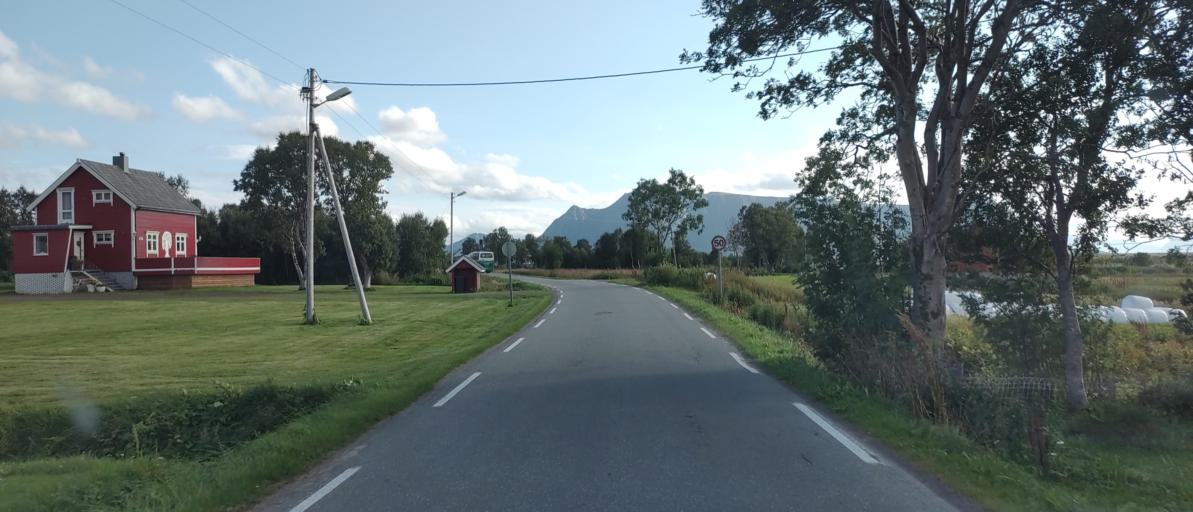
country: NO
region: Nordland
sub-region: Sortland
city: Sortland
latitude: 69.0404
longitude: 15.5161
